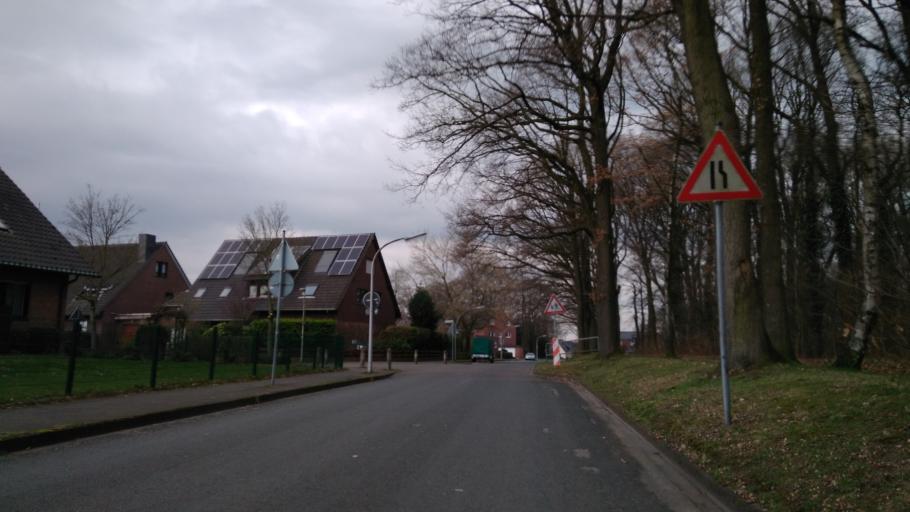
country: DE
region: North Rhine-Westphalia
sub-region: Regierungsbezirk Munster
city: Klein Reken
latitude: 51.7157
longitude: 7.0227
